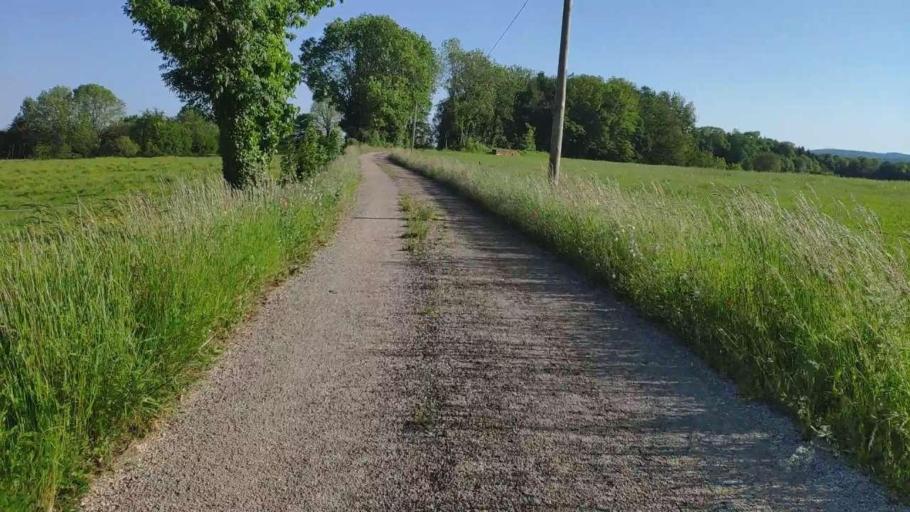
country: FR
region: Franche-Comte
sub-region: Departement du Jura
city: Perrigny
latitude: 46.7261
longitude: 5.6197
